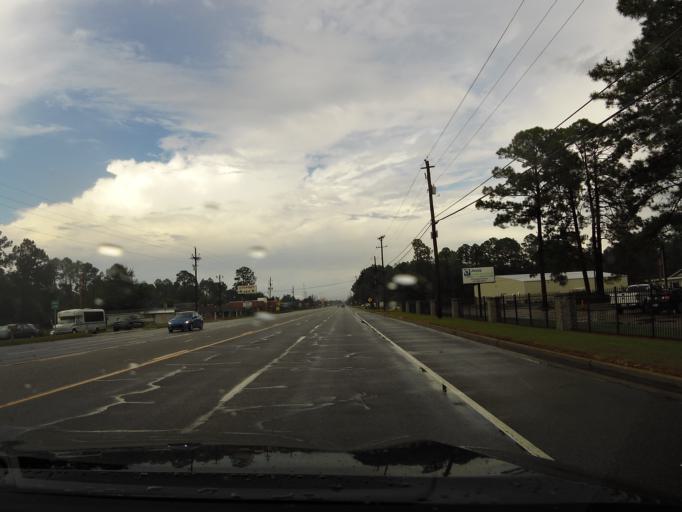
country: US
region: Georgia
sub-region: Wayne County
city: Jesup
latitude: 31.6429
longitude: -81.8580
